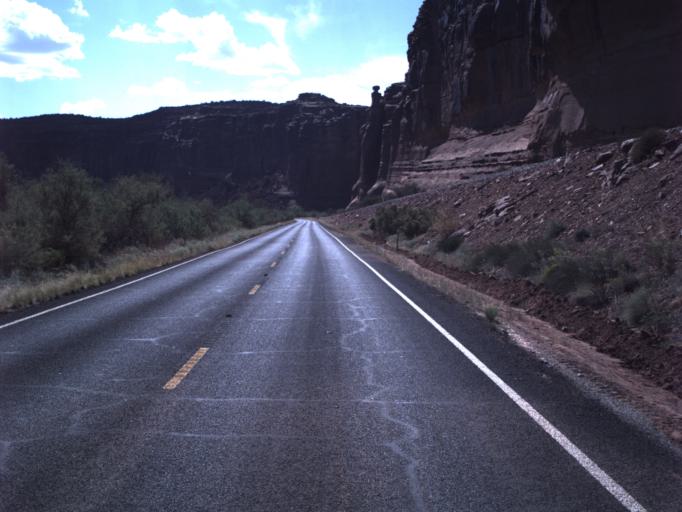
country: US
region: Utah
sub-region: Grand County
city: Moab
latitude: 38.5766
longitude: -109.6494
